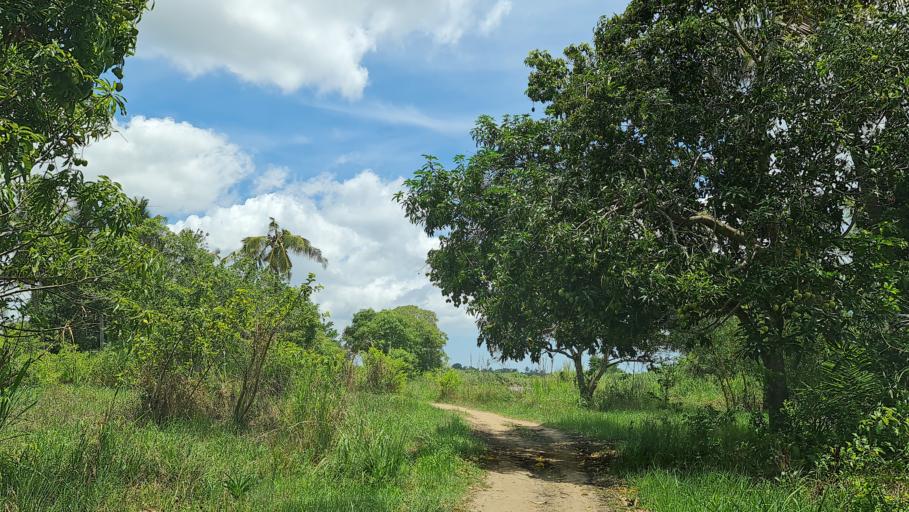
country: MZ
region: Zambezia
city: Quelimane
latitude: -17.5841
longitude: 37.3819
